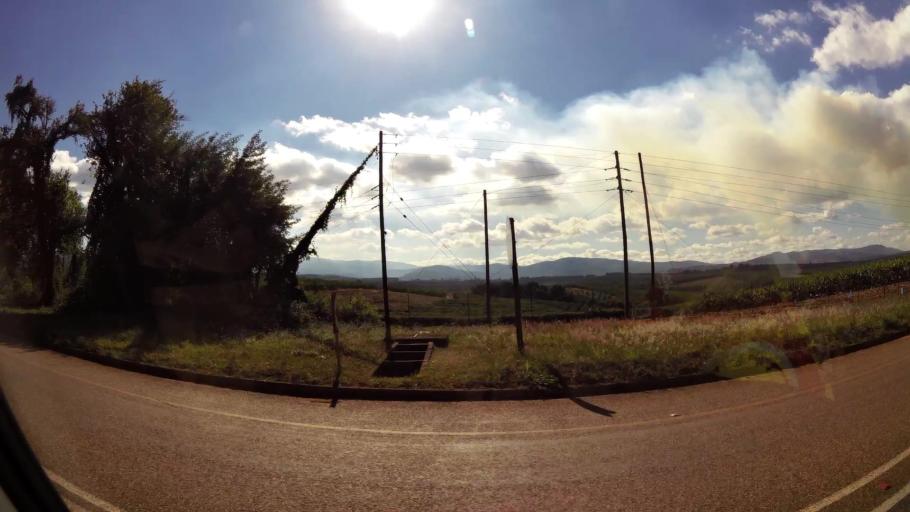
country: ZA
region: Limpopo
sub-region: Mopani District Municipality
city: Tzaneen
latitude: -23.8046
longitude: 30.1134
